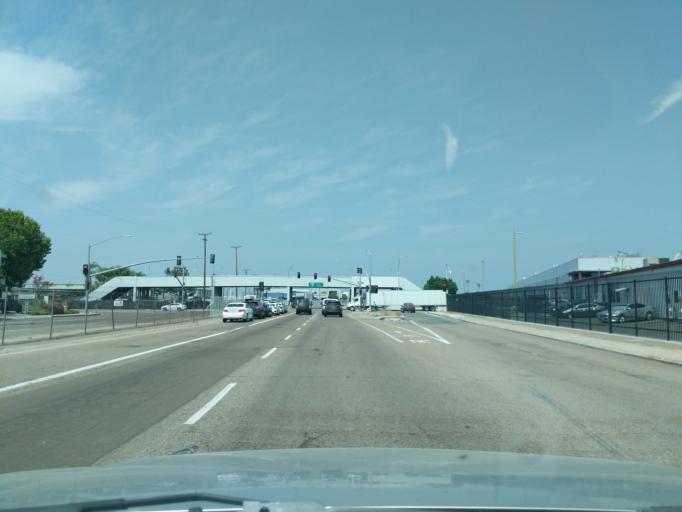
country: US
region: California
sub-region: San Diego County
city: San Diego
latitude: 32.7466
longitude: -117.1967
